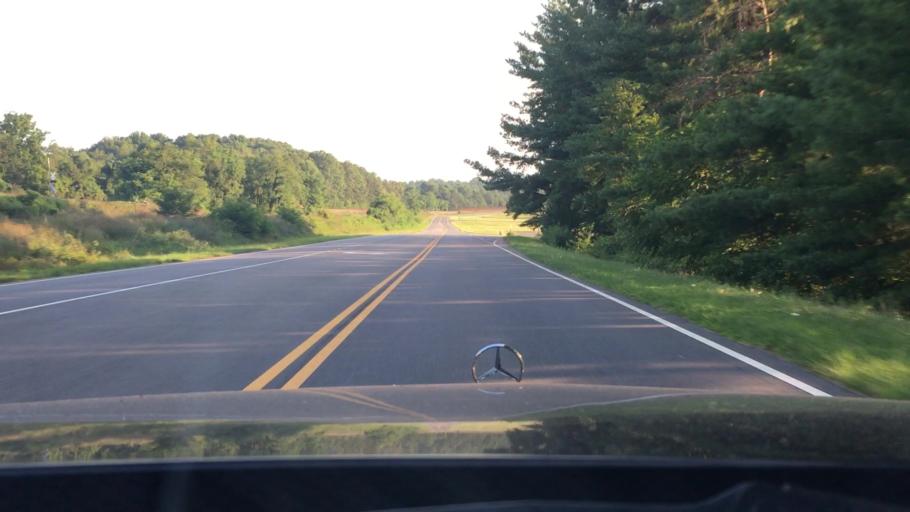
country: US
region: Virginia
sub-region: Pittsylvania County
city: Hurt
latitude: 37.0975
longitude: -79.3057
